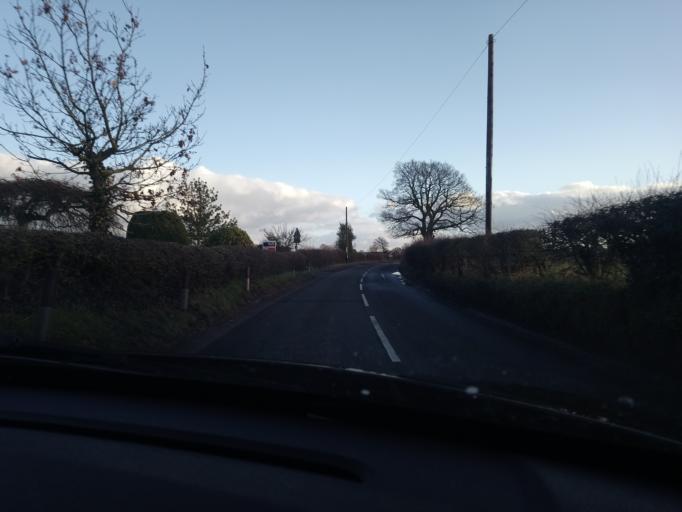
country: GB
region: England
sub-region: Shropshire
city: Petton
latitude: 52.8938
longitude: -2.7955
